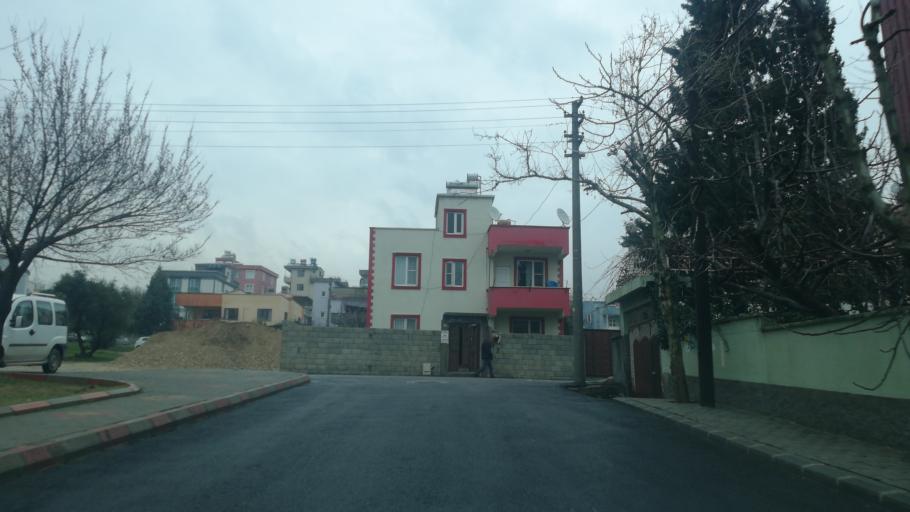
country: TR
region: Kahramanmaras
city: Kahramanmaras
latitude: 37.5690
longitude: 36.9437
